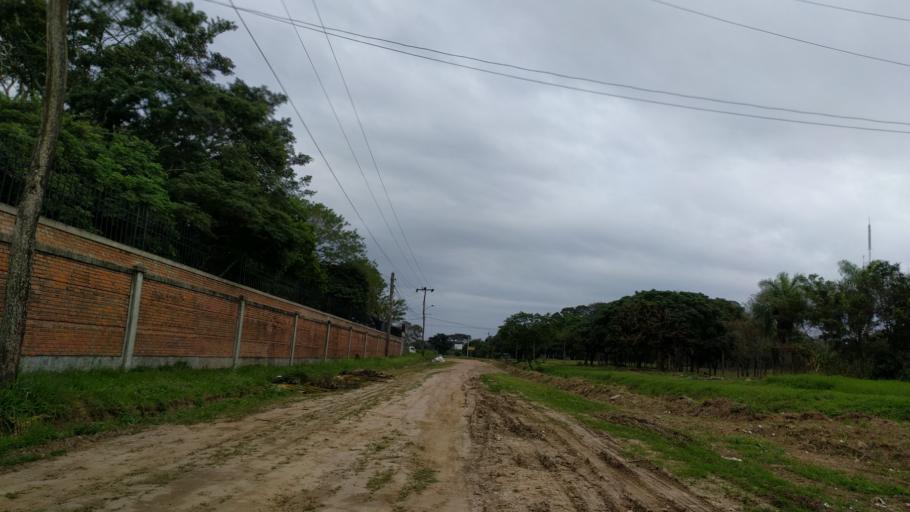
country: BO
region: Santa Cruz
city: Santa Cruz de la Sierra
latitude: -17.8101
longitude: -63.2317
